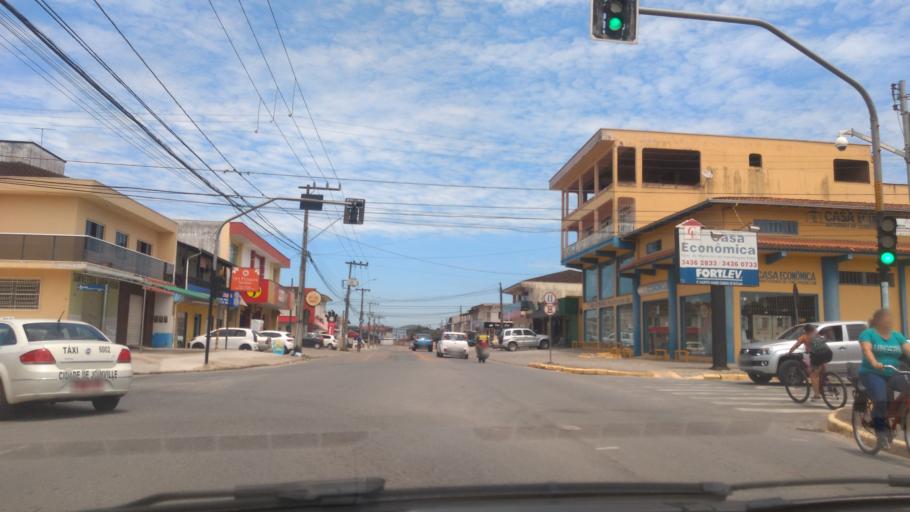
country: BR
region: Santa Catarina
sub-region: Joinville
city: Joinville
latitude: -26.3218
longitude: -48.8167
